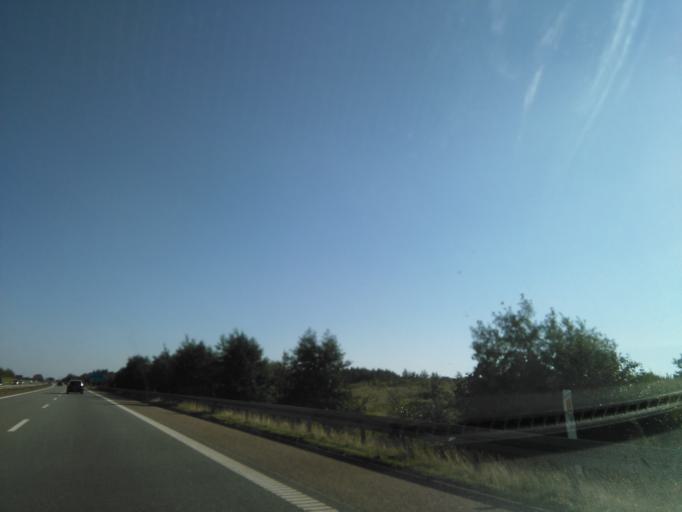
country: DK
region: Central Jutland
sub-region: Arhus Kommune
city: Hjortshoj
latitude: 56.2384
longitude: 10.2794
